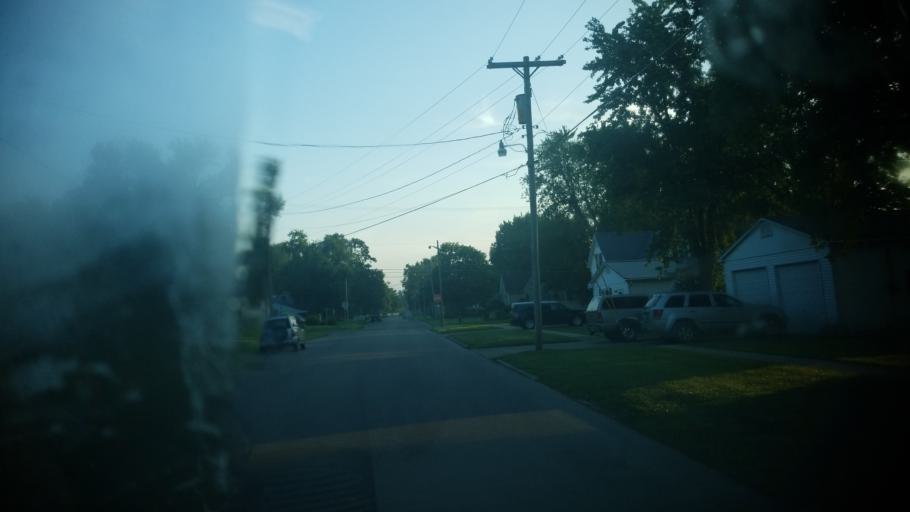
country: US
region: Illinois
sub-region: Wayne County
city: Fairfield
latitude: 38.3831
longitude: -88.3718
